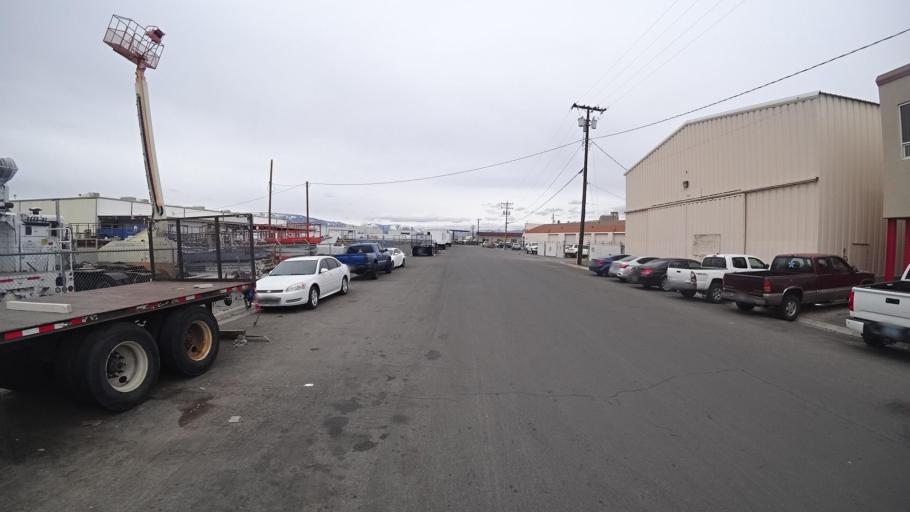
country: US
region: Nevada
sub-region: Washoe County
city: Sparks
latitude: 39.5289
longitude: -119.7468
